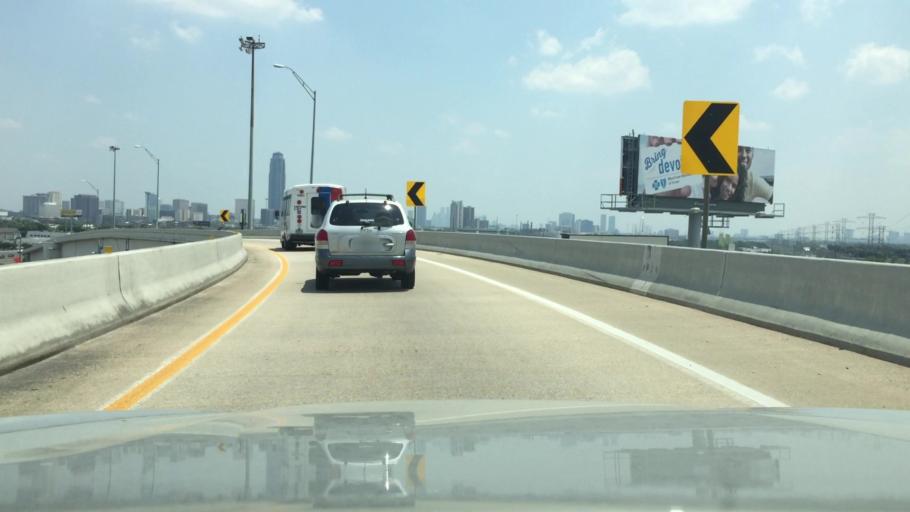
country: US
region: Texas
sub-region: Harris County
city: Bellaire
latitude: 29.7224
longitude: -95.4923
